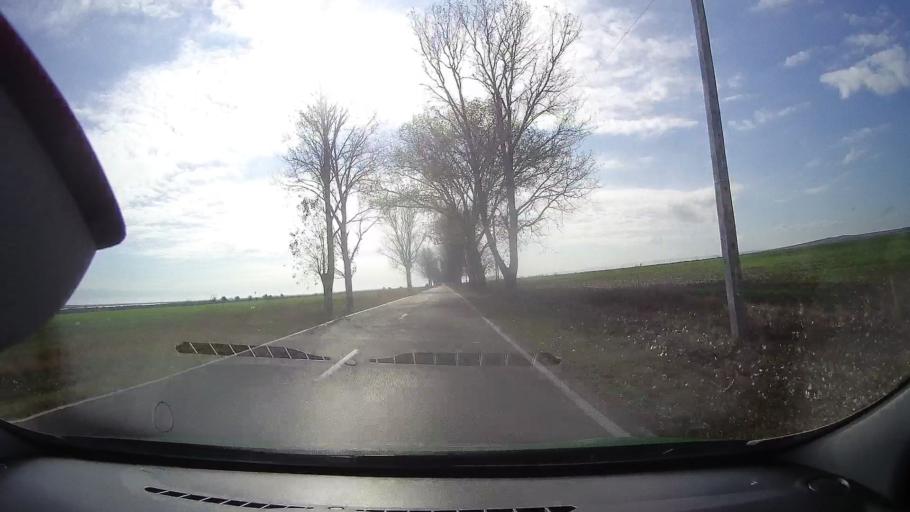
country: RO
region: Tulcea
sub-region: Comuna Valea Nucarilor
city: Agighiol
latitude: 45.0117
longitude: 28.8841
